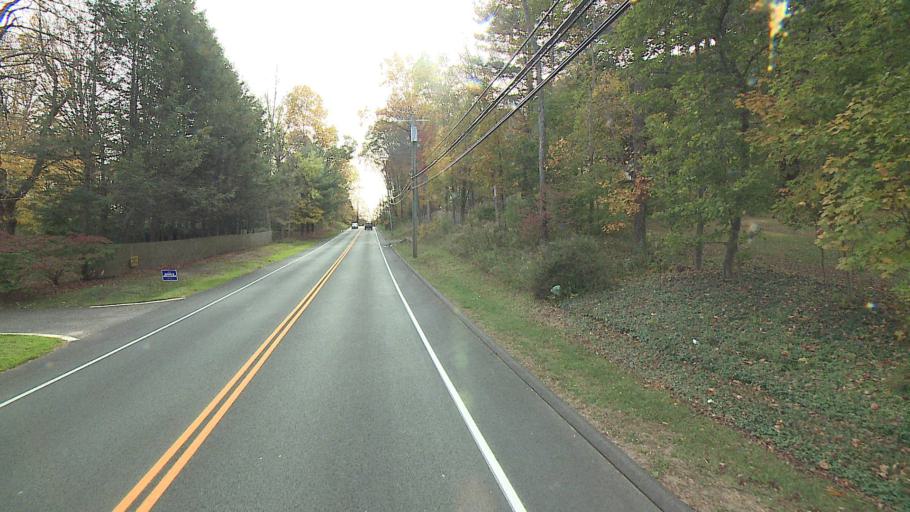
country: US
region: Connecticut
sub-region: Litchfield County
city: Canaan
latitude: 41.9761
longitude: -73.4272
